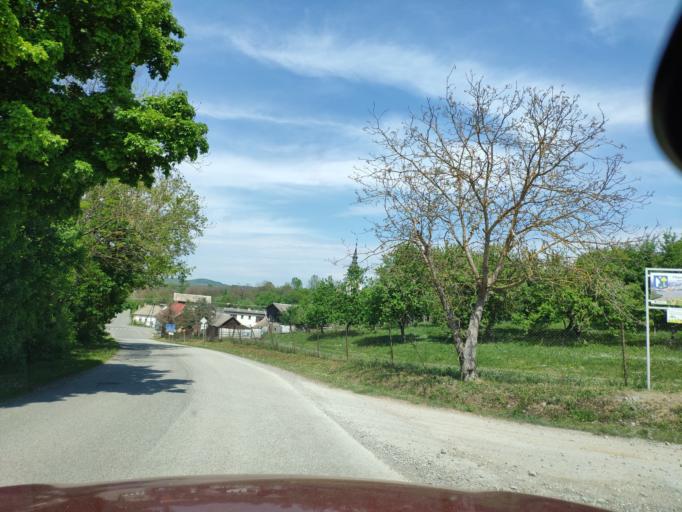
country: SK
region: Banskobystricky
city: Rimavska Sobota
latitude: 48.4688
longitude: 20.1020
